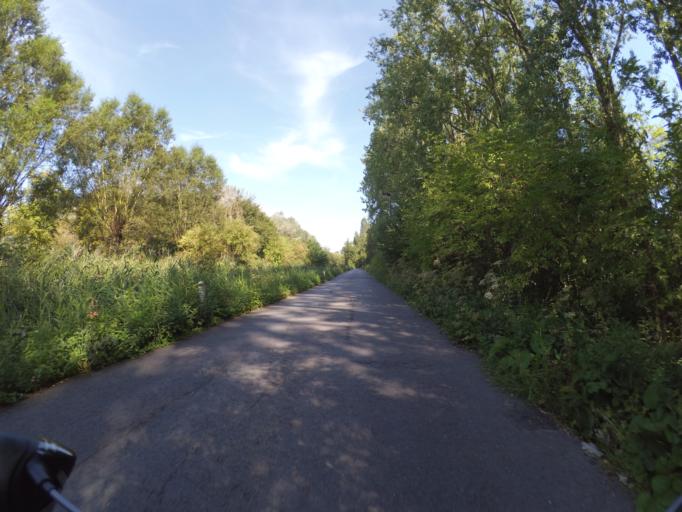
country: BE
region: Flanders
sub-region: Provincie Oost-Vlaanderen
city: Oudenaarde
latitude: 50.8451
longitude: 3.5978
